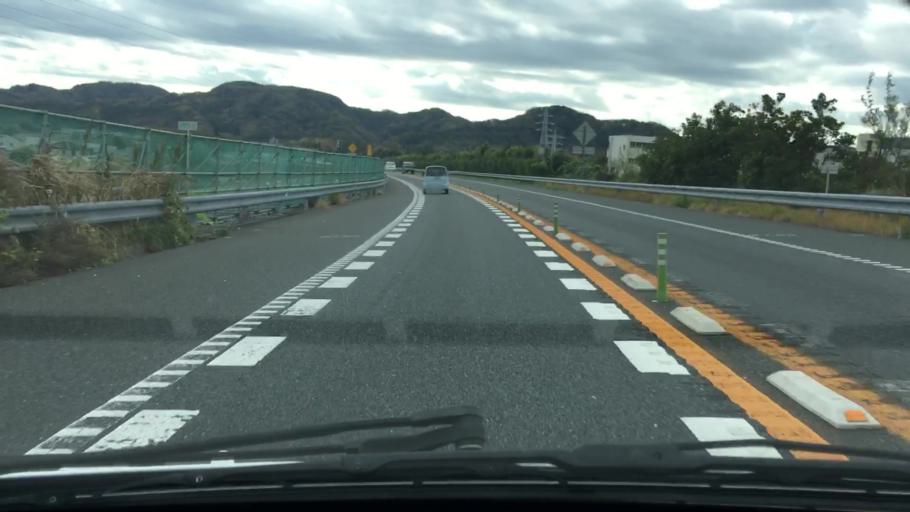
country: JP
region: Chiba
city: Kimitsu
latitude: 35.2217
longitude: 139.8846
